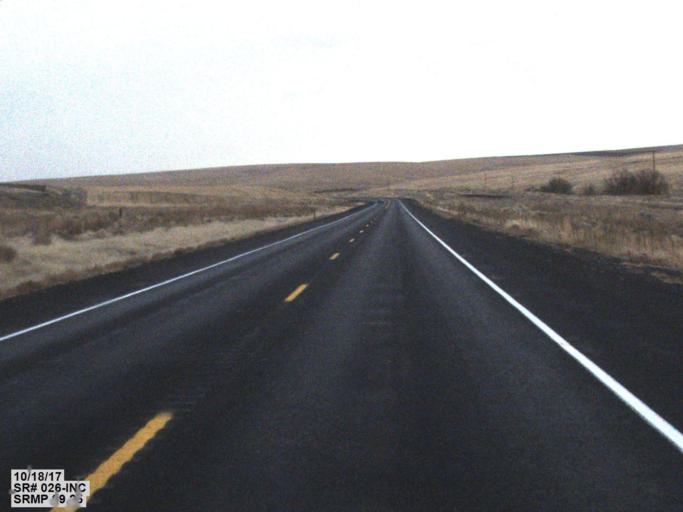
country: US
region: Washington
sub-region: Columbia County
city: Dayton
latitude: 46.7640
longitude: -117.9978
